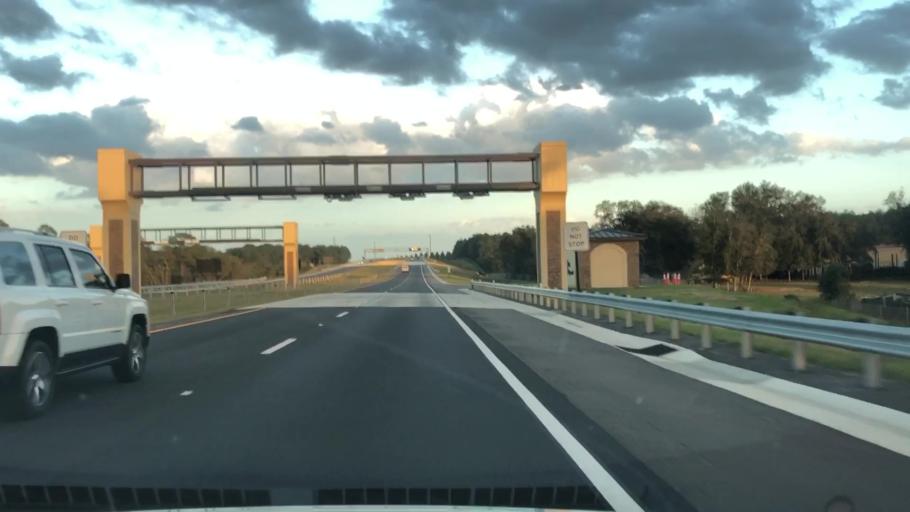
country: US
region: Florida
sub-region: Lake County
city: Mount Plymouth
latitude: 28.7757
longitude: -81.5422
